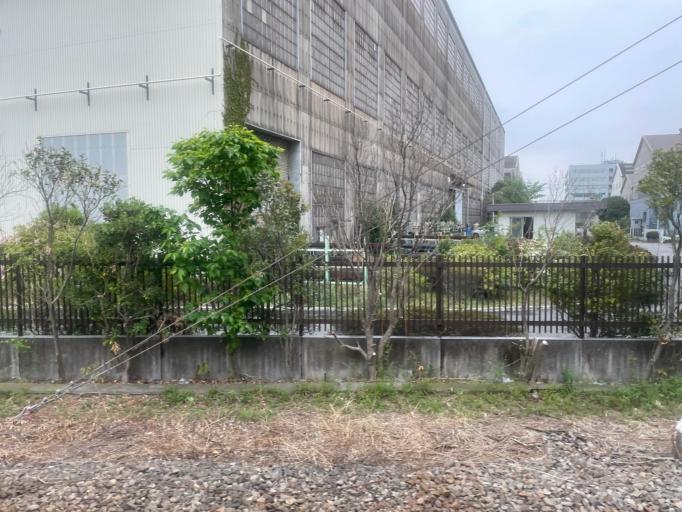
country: JP
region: Kanagawa
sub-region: Kawasaki-shi
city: Kawasaki
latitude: 35.5038
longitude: 139.7090
